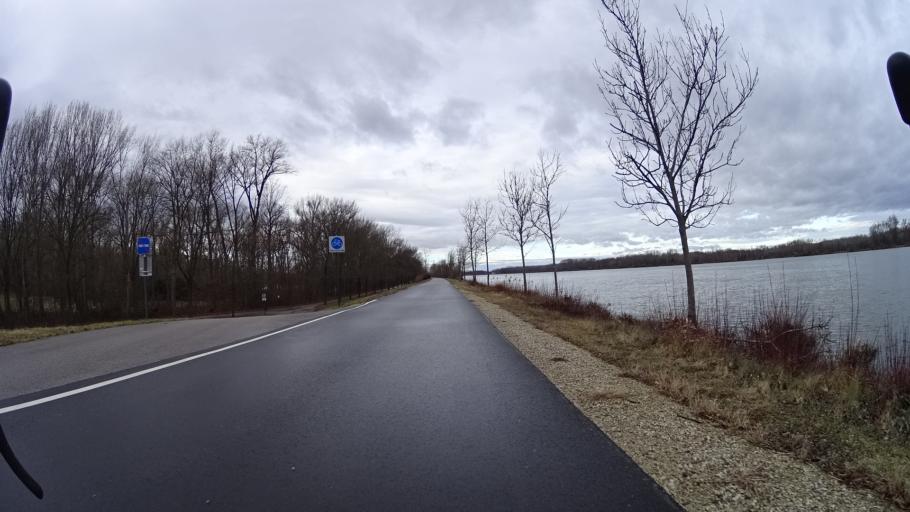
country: AT
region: Lower Austria
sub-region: Politischer Bezirk Tulln
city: Tulln
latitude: 48.3337
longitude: 16.0832
